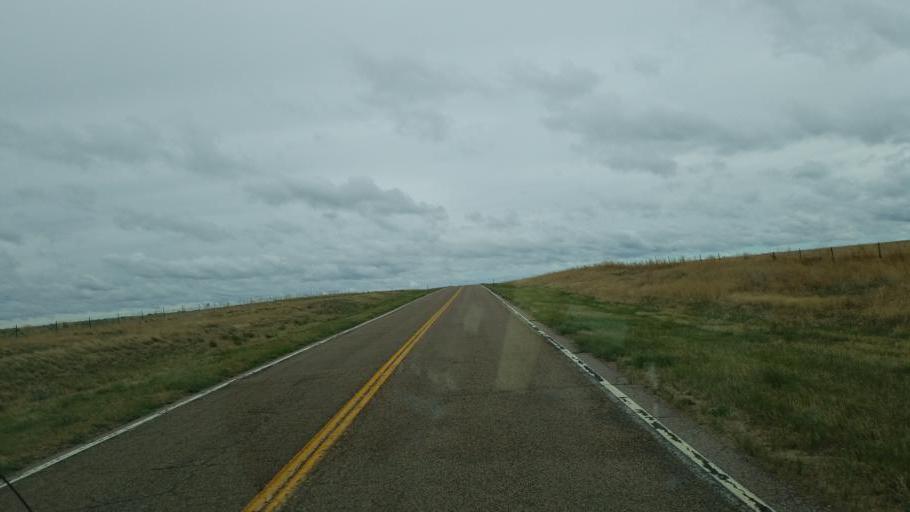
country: US
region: Colorado
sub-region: Lincoln County
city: Hugo
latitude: 38.8504
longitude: -103.4560
